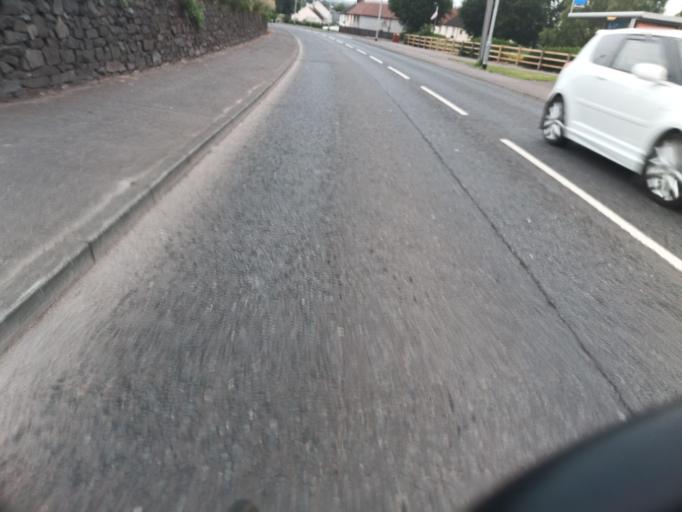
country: GB
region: Northern Ireland
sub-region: Ards District
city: Comber
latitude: 54.5525
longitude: -5.7356
